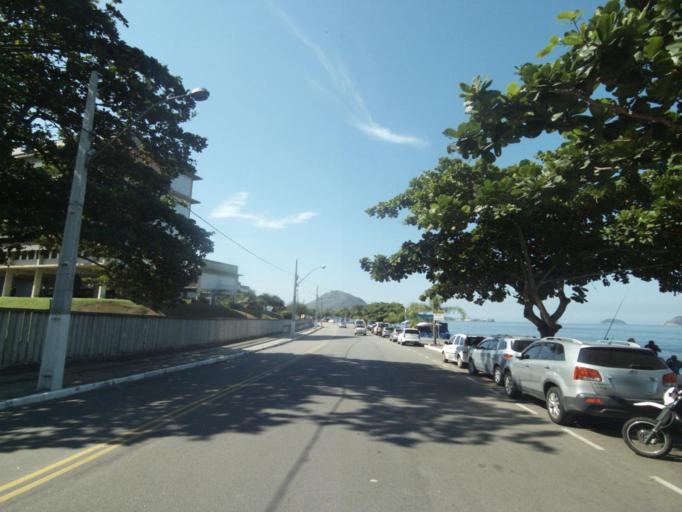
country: BR
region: Rio de Janeiro
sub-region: Niteroi
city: Niteroi
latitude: -22.9041
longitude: -43.1354
